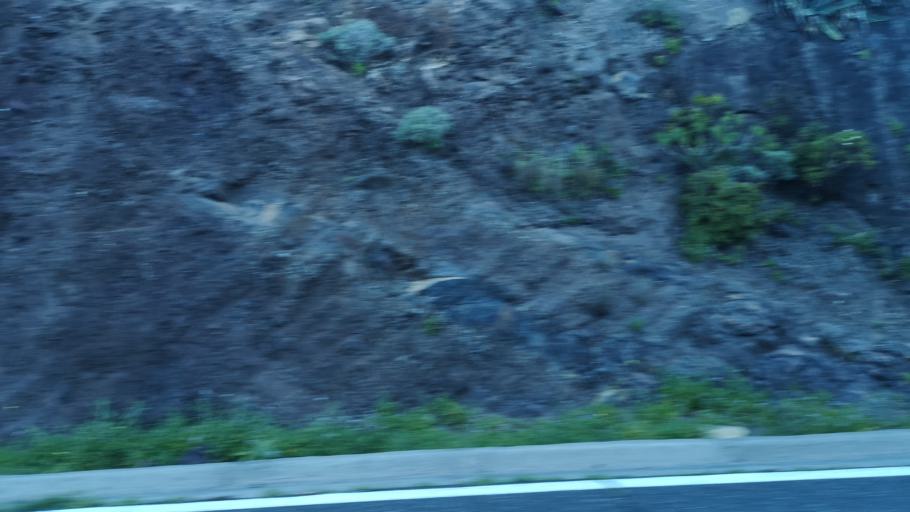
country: ES
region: Canary Islands
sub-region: Provincia de Santa Cruz de Tenerife
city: Alajero
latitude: 28.0821
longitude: -17.2457
